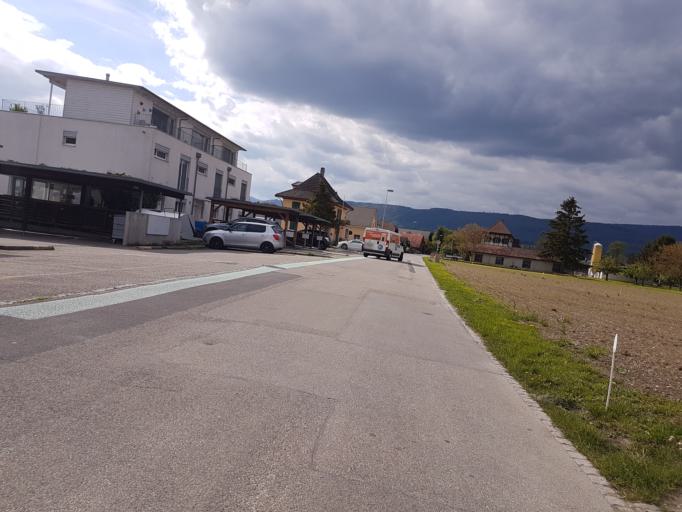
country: CH
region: Bern
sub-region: Biel/Bienne District
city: Meinisberg
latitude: 47.1419
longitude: 7.3712
